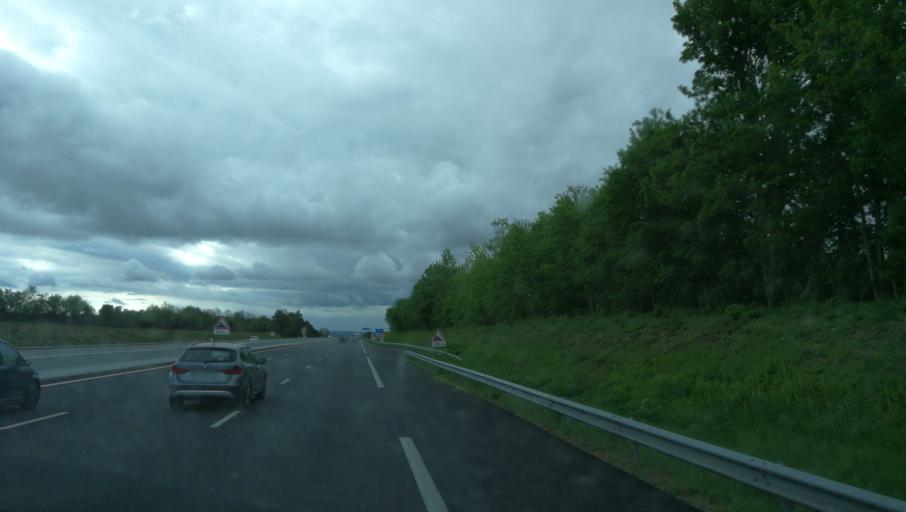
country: FR
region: Ile-de-France
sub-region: Departement de Seine-et-Marne
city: La Chapelle-la-Reine
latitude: 48.3153
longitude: 2.6276
